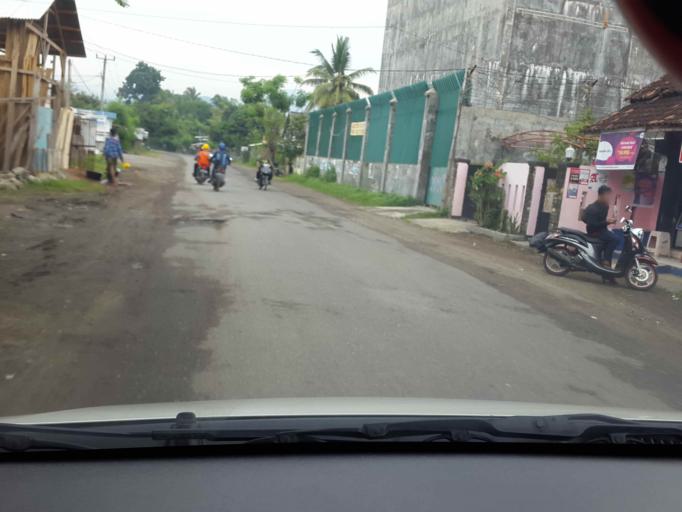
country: ID
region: West Java
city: Cidadap
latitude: -7.0122
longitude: 106.5438
